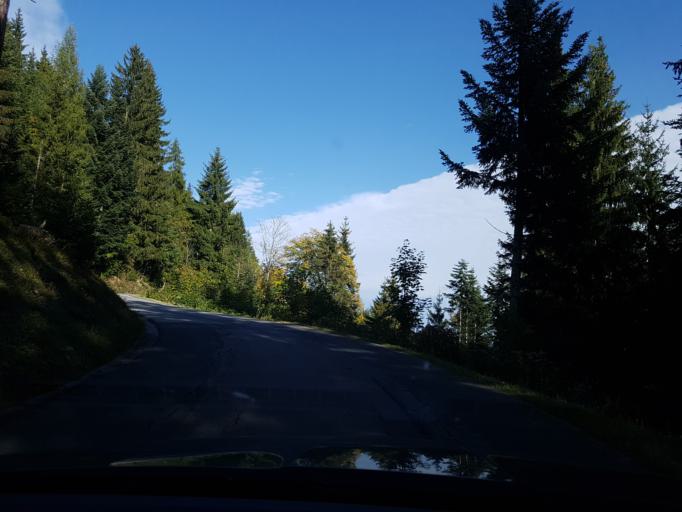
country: AT
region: Salzburg
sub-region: Politischer Bezirk Sankt Johann im Pongau
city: Radstadt
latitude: 47.3931
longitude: 13.4825
